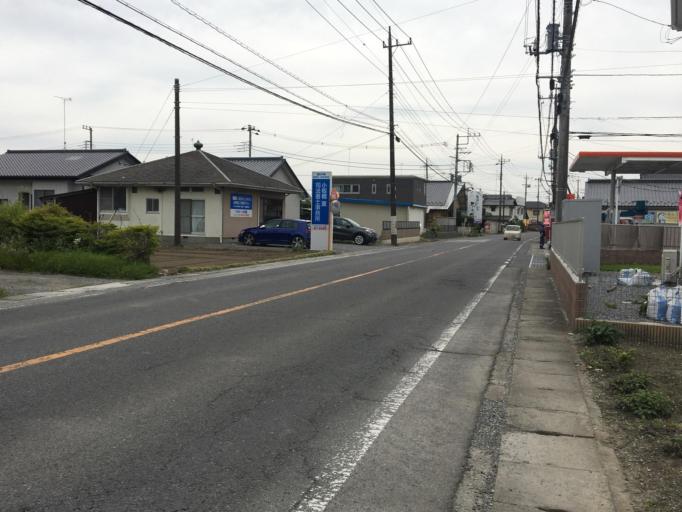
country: JP
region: Tochigi
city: Tochigi
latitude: 36.4087
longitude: 139.7447
